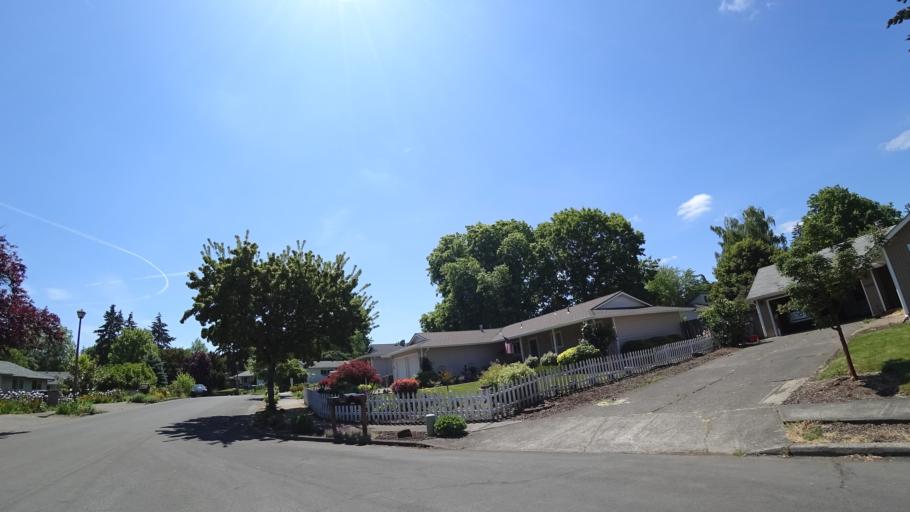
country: US
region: Oregon
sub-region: Washington County
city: King City
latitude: 45.4312
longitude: -122.8083
